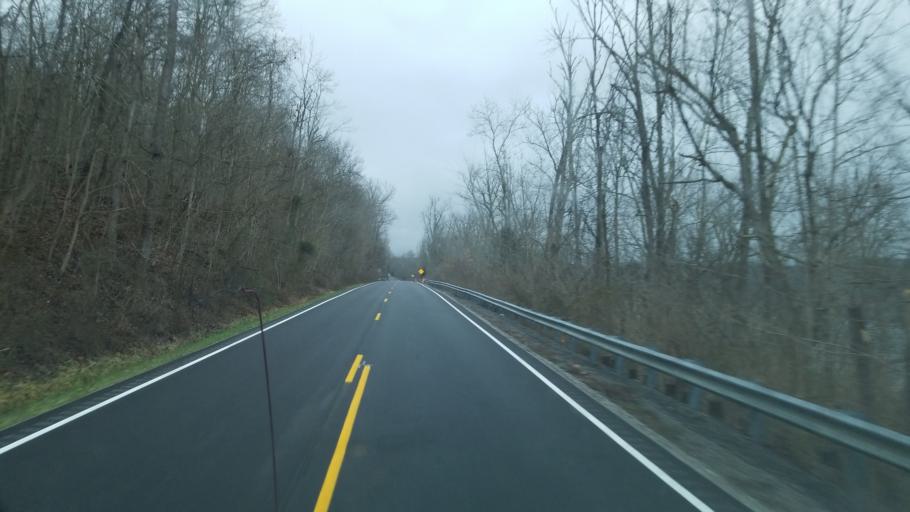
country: US
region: Kentucky
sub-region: Bracken County
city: Augusta
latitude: 38.7712
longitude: -83.9323
